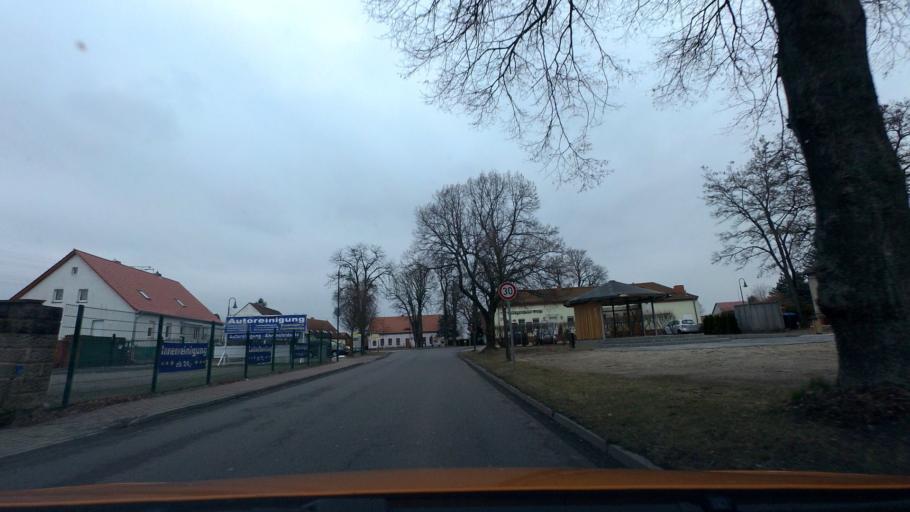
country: DE
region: Brandenburg
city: Ahrensfelde
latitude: 52.5628
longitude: 13.5894
